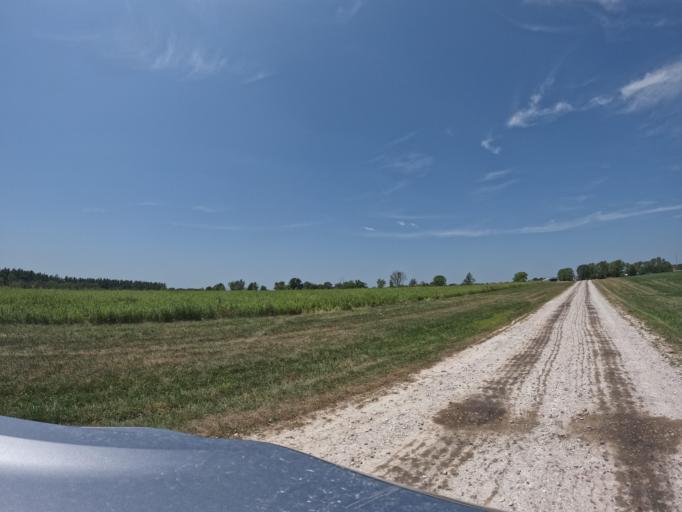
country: US
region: Iowa
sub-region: Henry County
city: Mount Pleasant
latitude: 40.9404
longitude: -91.5859
